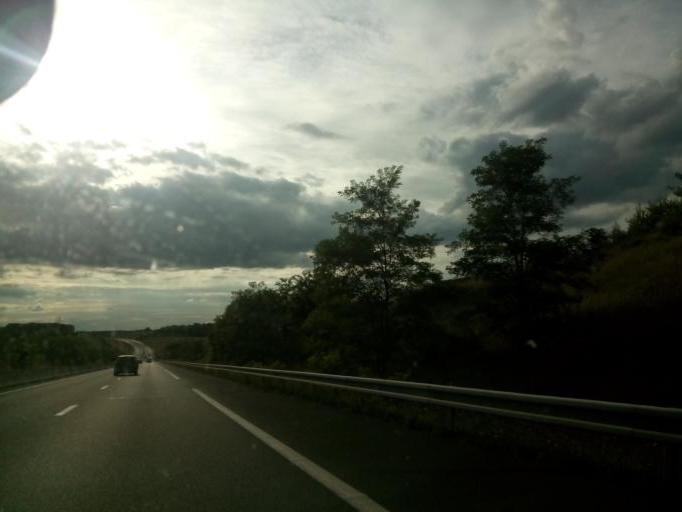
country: FR
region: Centre
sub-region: Departement du Loir-et-Cher
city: Saint-Georges-sur-Cher
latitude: 47.2937
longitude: 1.1189
